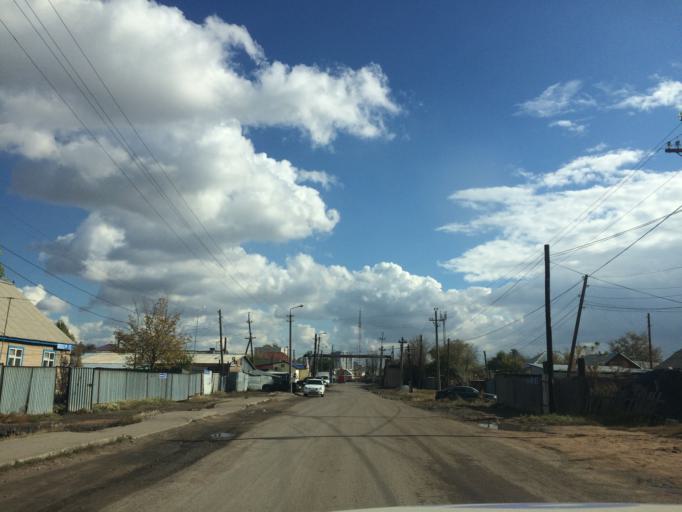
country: KZ
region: Astana Qalasy
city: Astana
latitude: 51.1916
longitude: 71.3924
